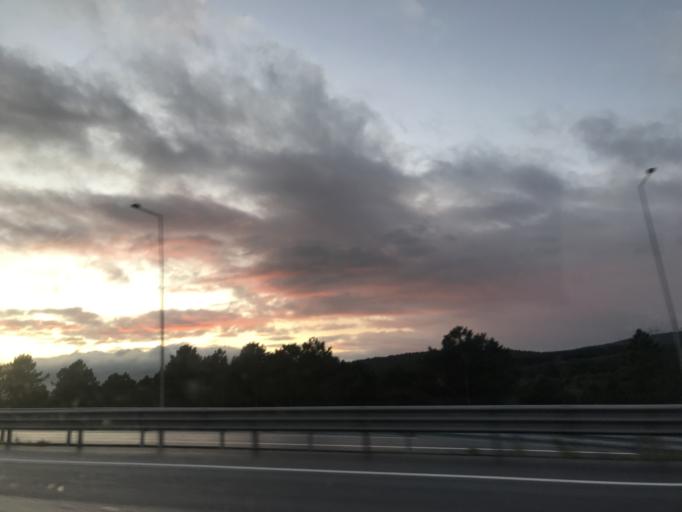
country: TR
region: Istanbul
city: Sultanbeyli
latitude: 40.9621
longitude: 29.3203
